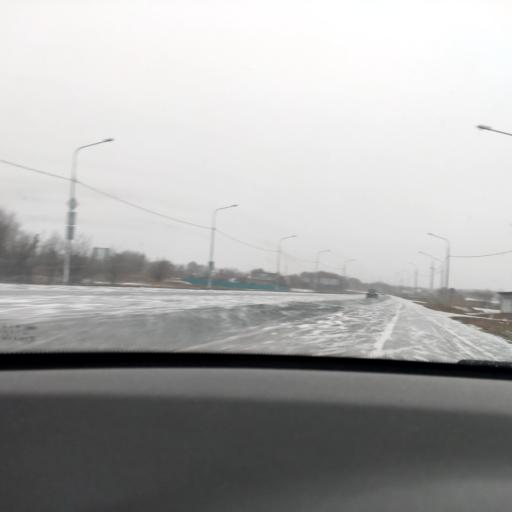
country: RU
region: Samara
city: Krasnoarmeyskoye
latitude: 52.8897
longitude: 49.9732
